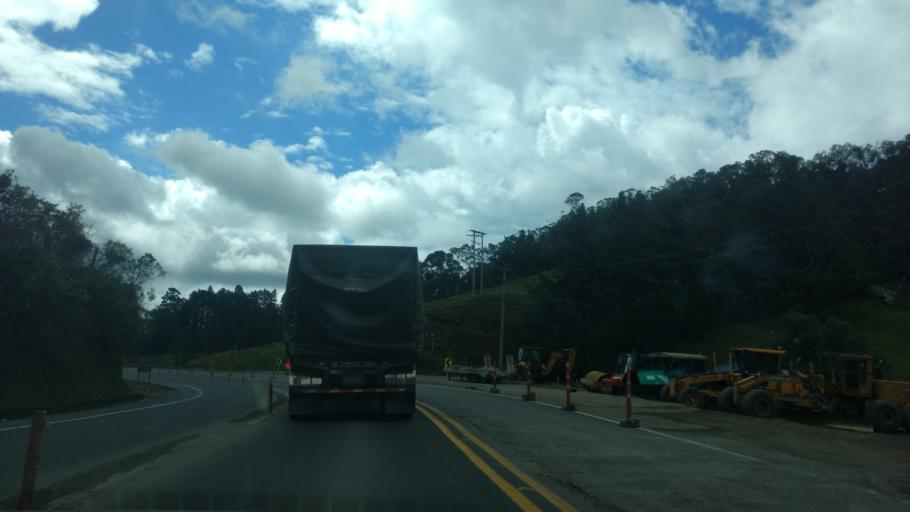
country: CO
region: Cundinamarca
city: San Francisco
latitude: 4.9304
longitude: -74.2967
